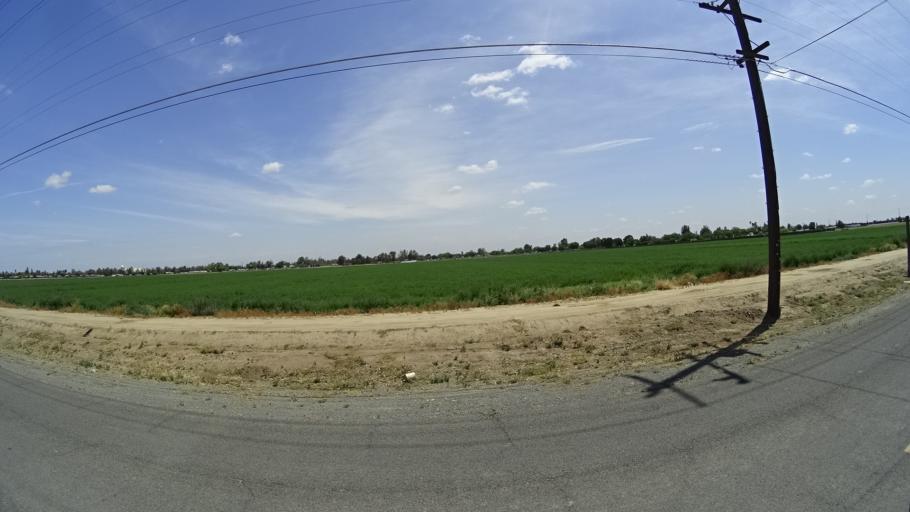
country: US
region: California
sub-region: Kings County
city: Home Garden
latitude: 36.3038
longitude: -119.6460
